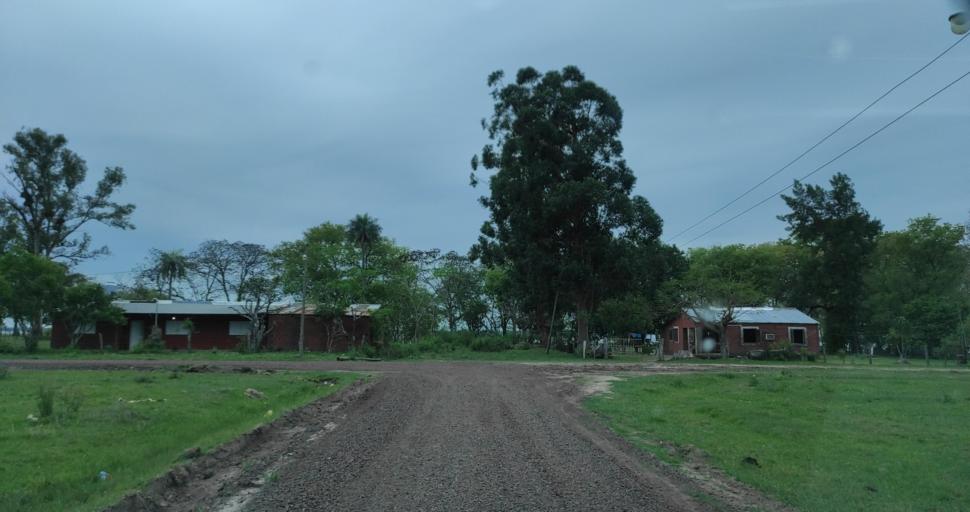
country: PY
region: Neembucu
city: Cerrito
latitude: -27.3720
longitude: -57.6538
